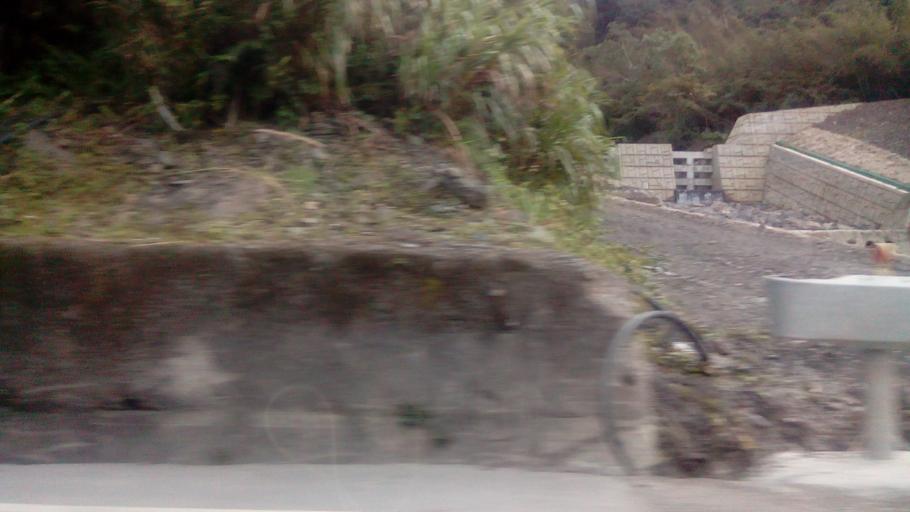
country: TW
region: Taiwan
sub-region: Yilan
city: Yilan
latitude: 24.5386
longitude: 121.4559
